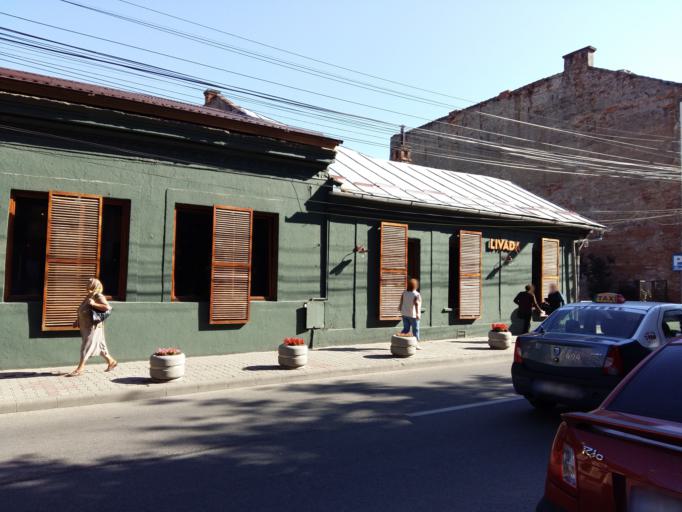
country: RO
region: Cluj
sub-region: Municipiul Cluj-Napoca
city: Cluj-Napoca
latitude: 46.7657
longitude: 23.5824
